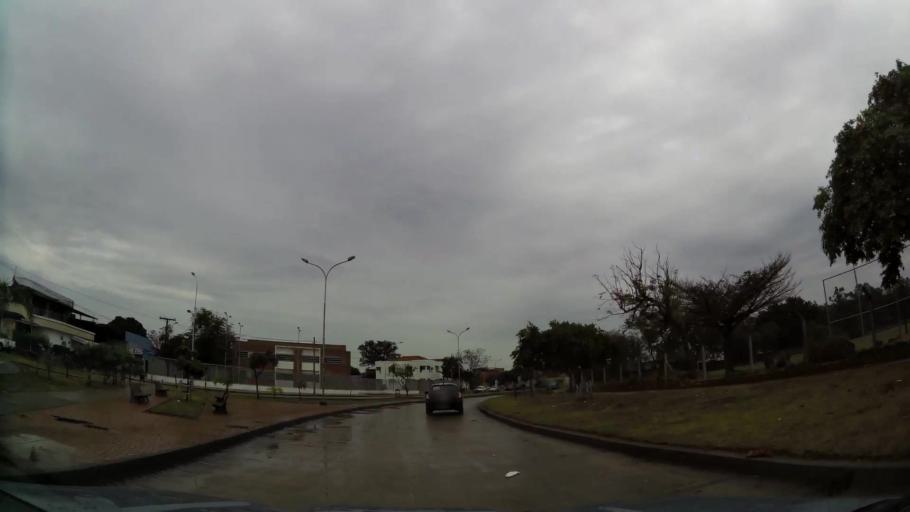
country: BO
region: Santa Cruz
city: Santa Cruz de la Sierra
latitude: -17.8104
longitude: -63.1954
